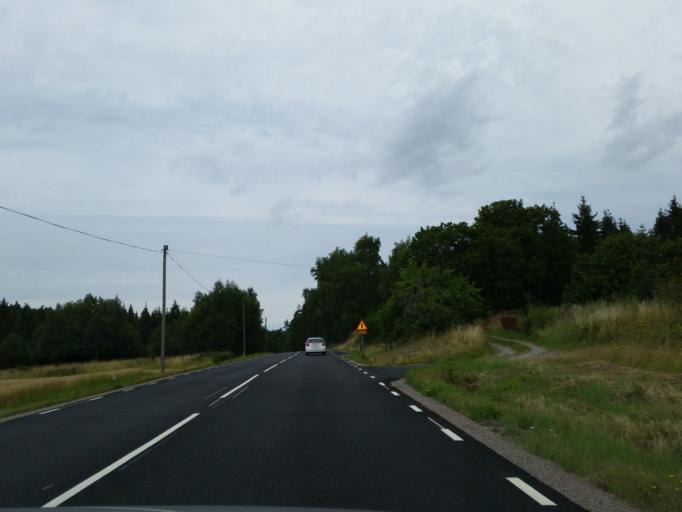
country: SE
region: Soedermanland
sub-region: Strangnas Kommun
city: Mariefred
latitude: 59.2607
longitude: 17.1685
